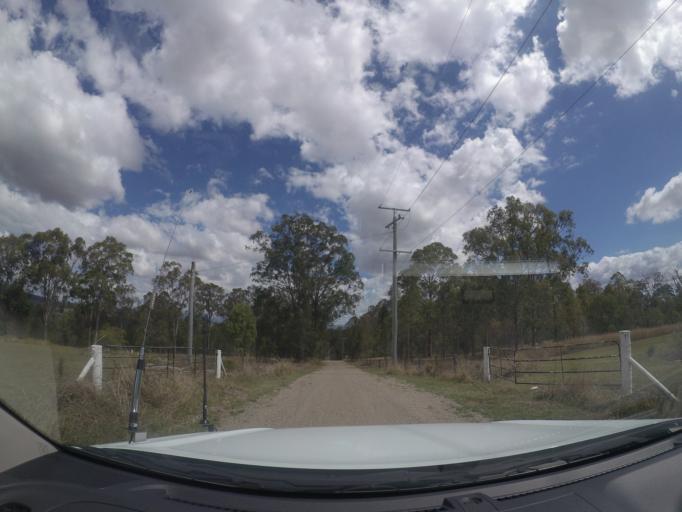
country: AU
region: Queensland
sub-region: Logan
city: Cedar Vale
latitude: -27.8969
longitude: 153.0011
